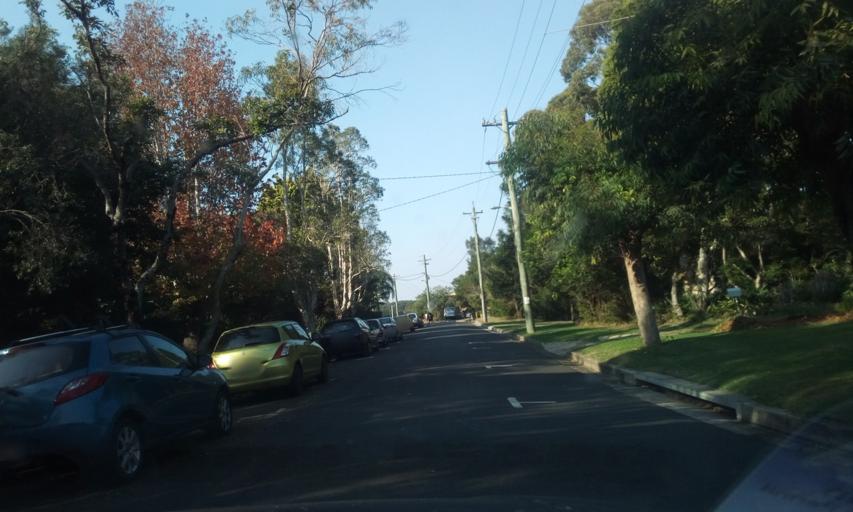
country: AU
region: New South Wales
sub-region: Wollongong
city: Mount Ousley
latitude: -34.4027
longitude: 150.8744
